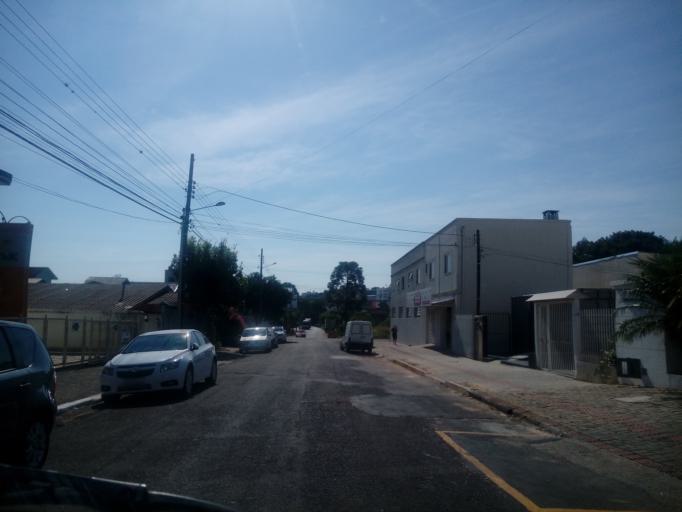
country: BR
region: Santa Catarina
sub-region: Chapeco
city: Chapeco
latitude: -27.0878
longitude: -52.6253
